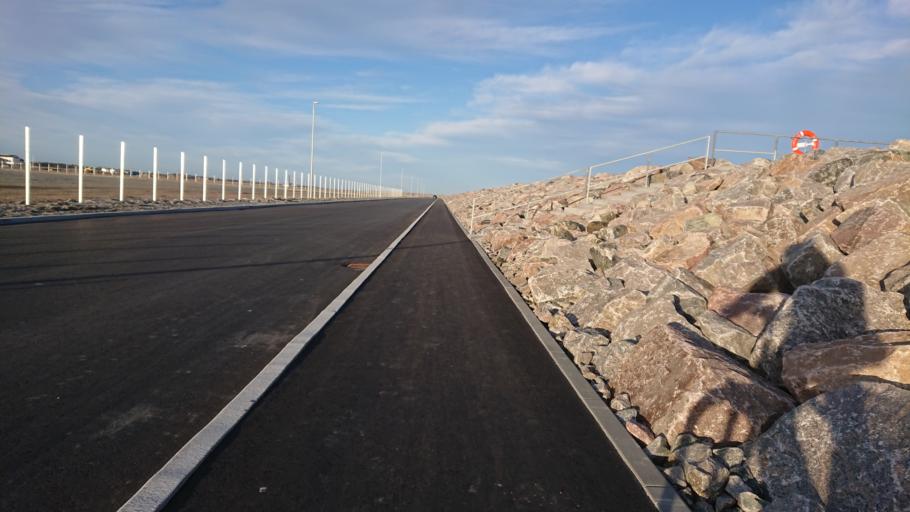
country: DK
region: North Denmark
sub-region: Frederikshavn Kommune
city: Skagen
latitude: 57.7160
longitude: 10.6019
